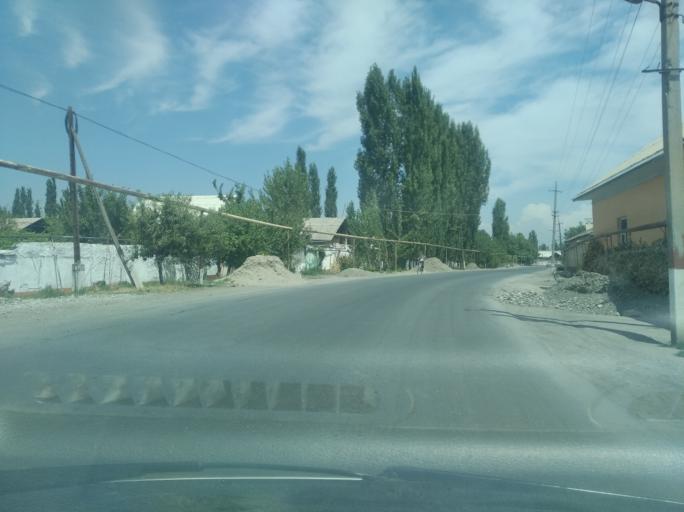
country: UZ
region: Andijon
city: Khujaobod
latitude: 40.6257
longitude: 72.4498
